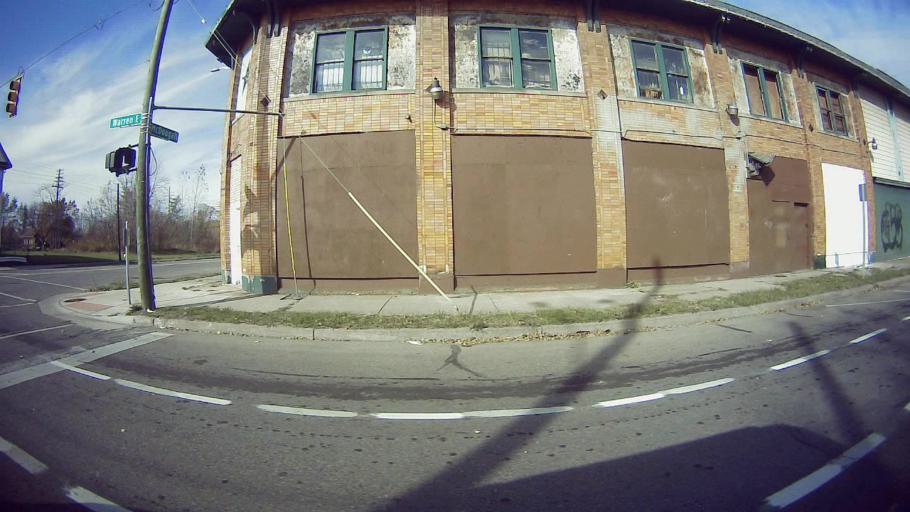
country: US
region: Michigan
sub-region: Wayne County
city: Hamtramck
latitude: 42.3674
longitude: -83.0360
